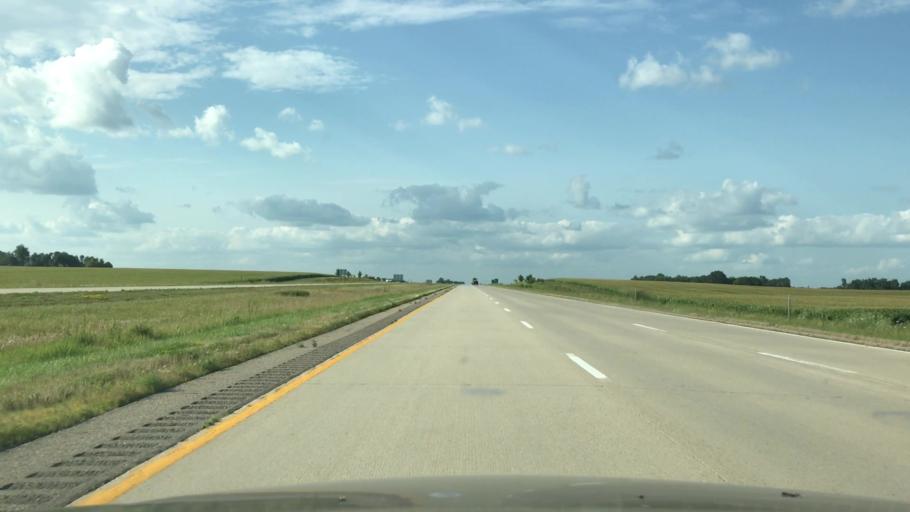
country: US
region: Iowa
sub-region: Osceola County
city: Sibley
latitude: 43.4103
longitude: -95.7170
